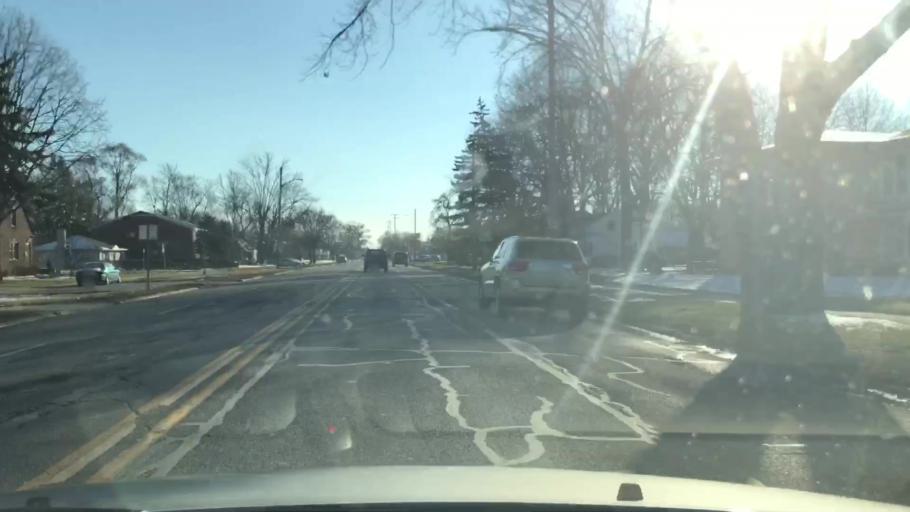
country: US
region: Michigan
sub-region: Oakland County
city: Clawson
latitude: 42.5315
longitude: -83.1365
